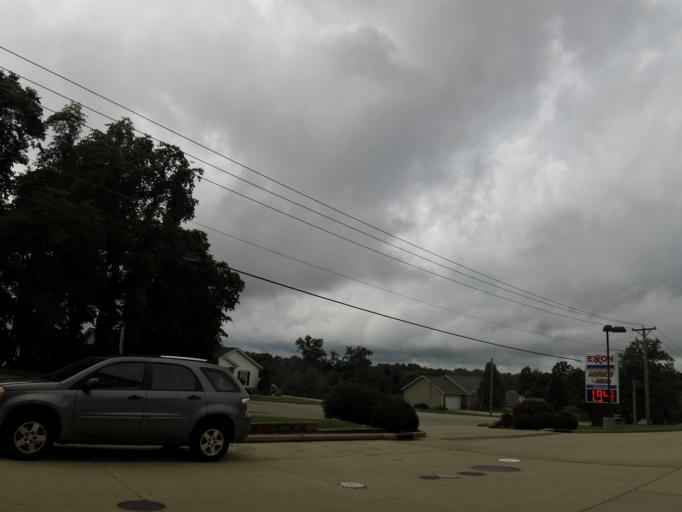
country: US
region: Missouri
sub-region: Cape Girardeau County
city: Cape Girardeau
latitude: 37.3383
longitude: -89.5537
